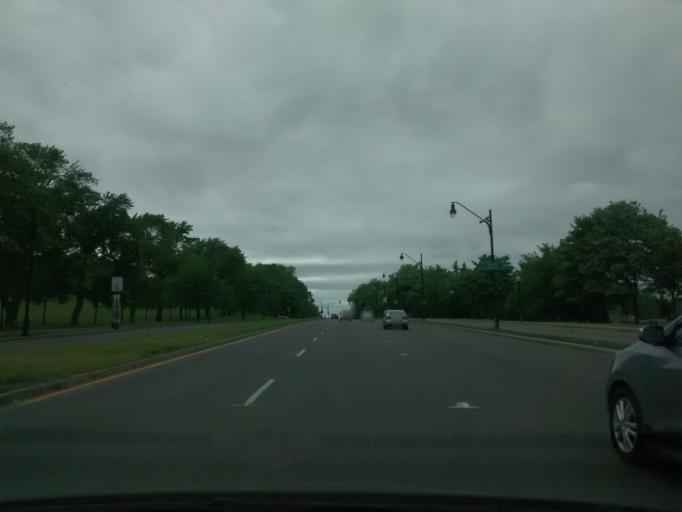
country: CA
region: Quebec
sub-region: Montreal
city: Montreal
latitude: 45.5122
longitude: -73.5792
